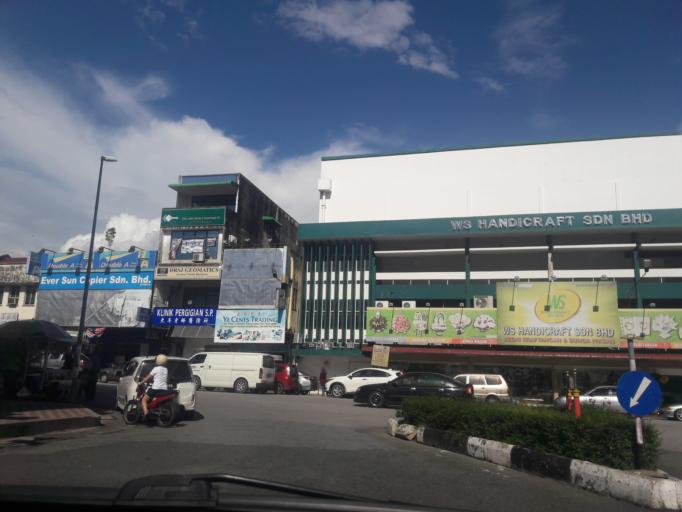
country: MY
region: Kedah
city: Sungai Petani
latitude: 5.6407
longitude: 100.4870
